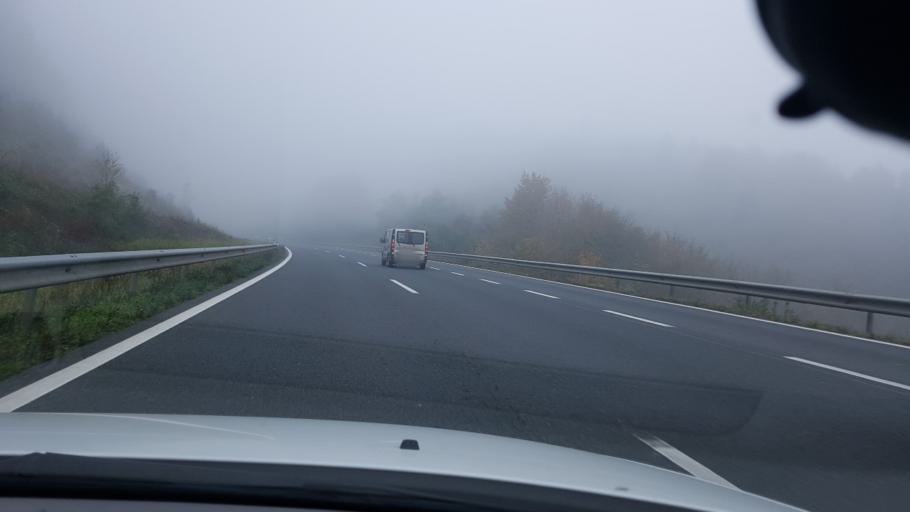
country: SI
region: Grosuplje
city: Grosuplje
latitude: 45.9706
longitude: 14.7221
